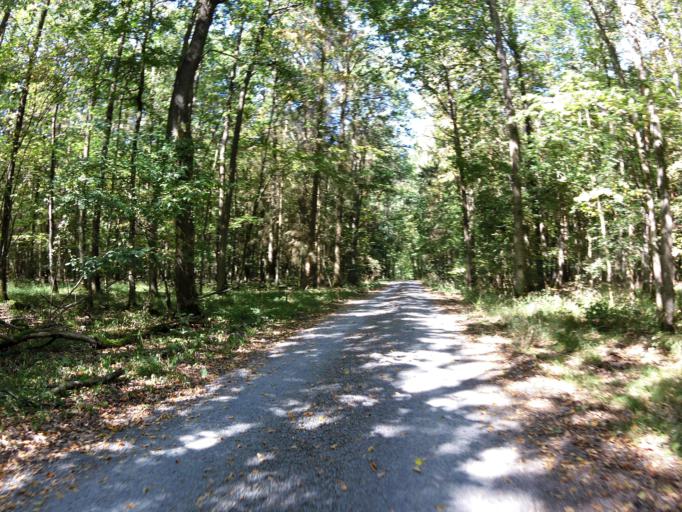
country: DE
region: Bavaria
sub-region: Regierungsbezirk Unterfranken
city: Gadheim
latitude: 49.8556
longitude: 9.8939
